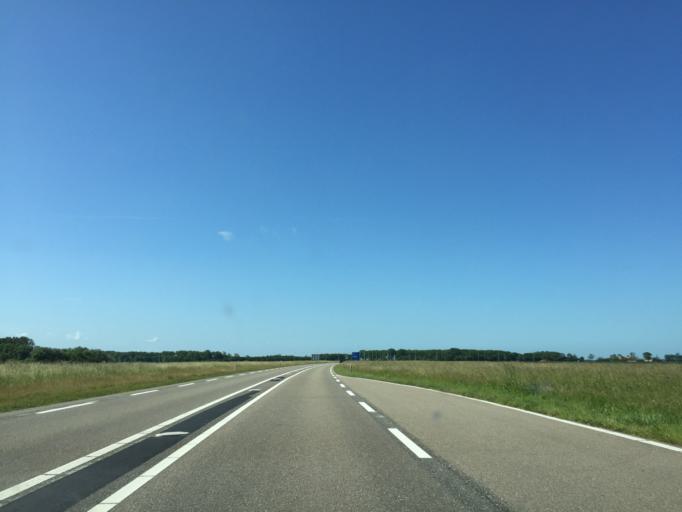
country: NL
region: Zeeland
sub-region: Schouwen-Duiveland
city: Scharendijke
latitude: 51.7107
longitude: 3.8125
